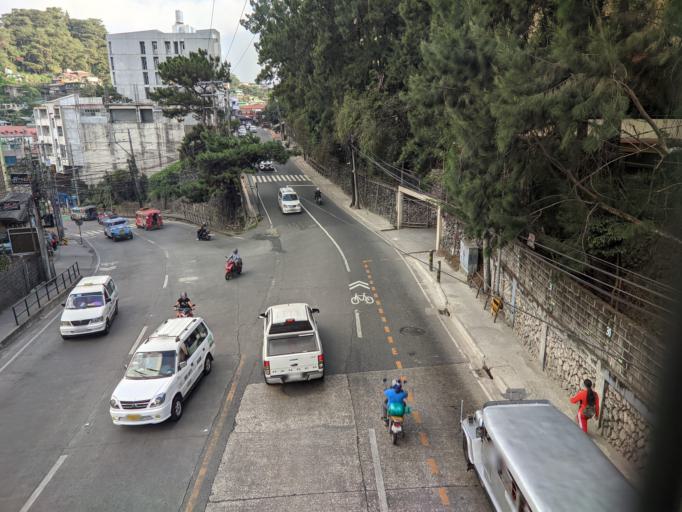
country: PH
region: Cordillera
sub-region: Baguio City
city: Baguio
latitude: 16.4196
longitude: 120.5979
